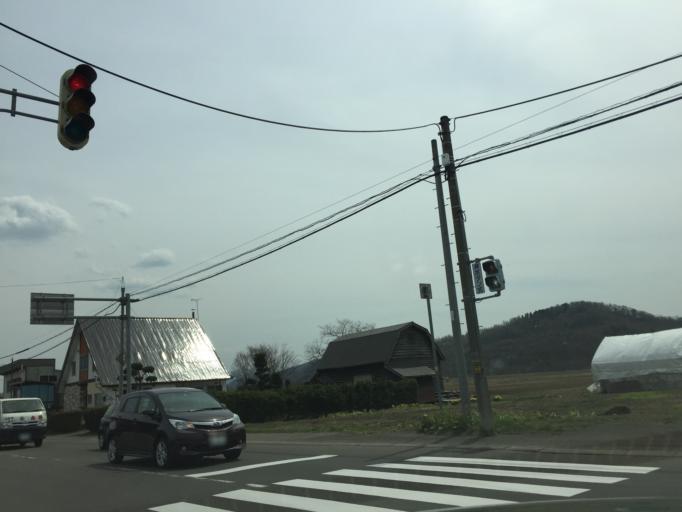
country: JP
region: Hokkaido
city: Ashibetsu
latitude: 43.5434
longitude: 142.1577
